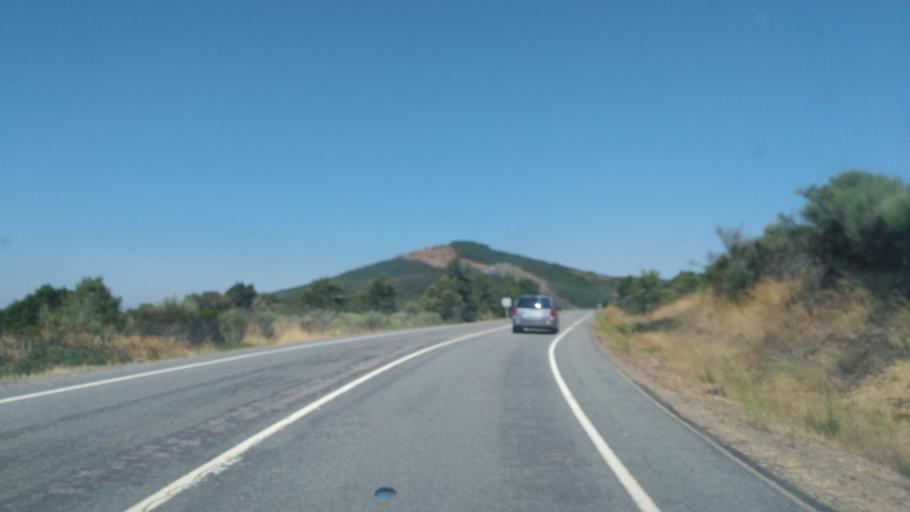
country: ES
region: Castille and Leon
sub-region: Provincia de Salamanca
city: Cereceda de la Sierra
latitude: 40.5689
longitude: -6.0755
